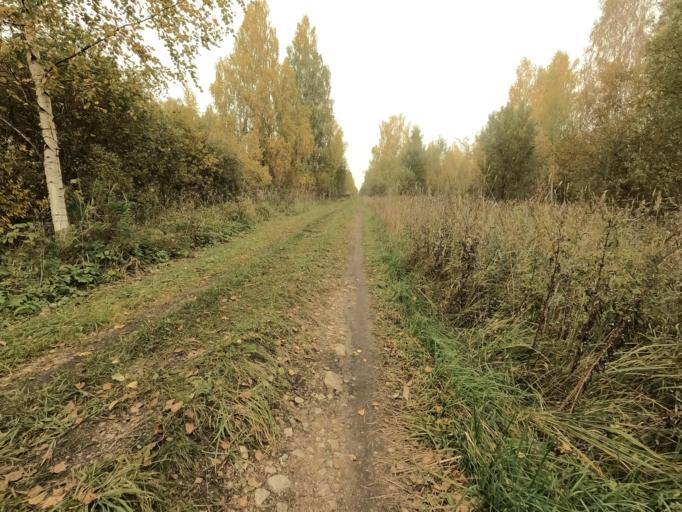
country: RU
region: Novgorod
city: Pankovka
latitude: 58.8818
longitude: 30.9439
